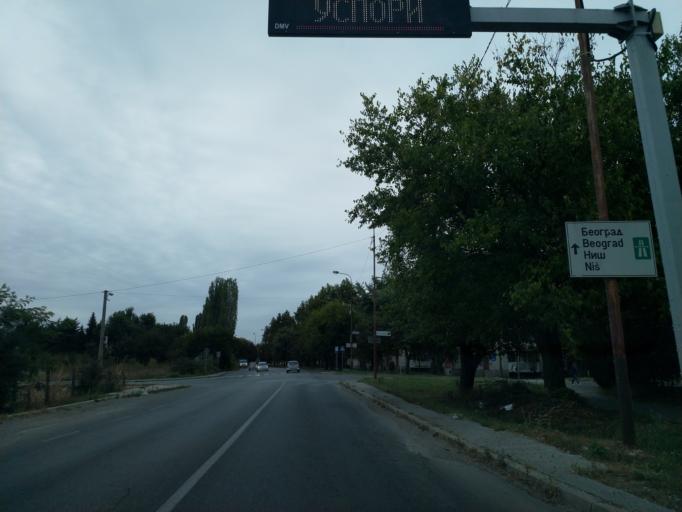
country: RS
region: Central Serbia
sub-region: Pomoravski Okrug
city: Jagodina
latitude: 43.9869
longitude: 21.2419
